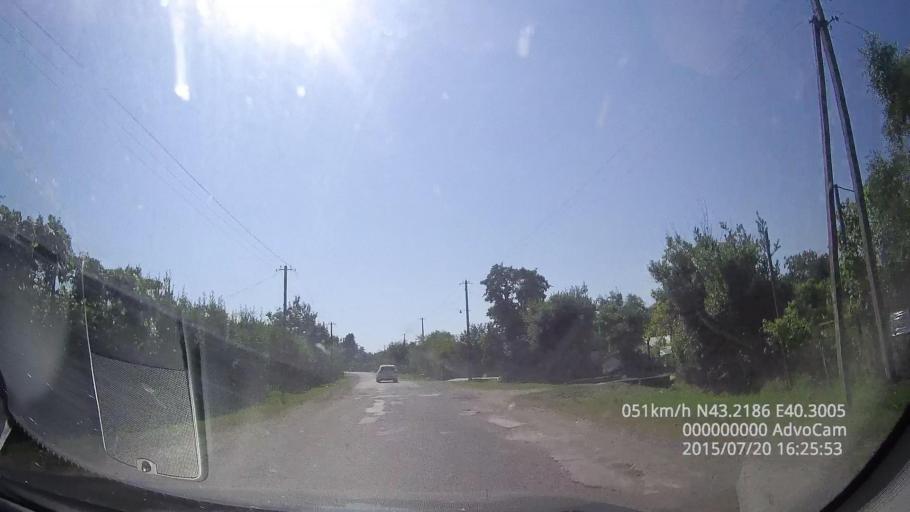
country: GE
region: Abkhazia
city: Gagra
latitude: 43.2186
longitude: 40.2999
